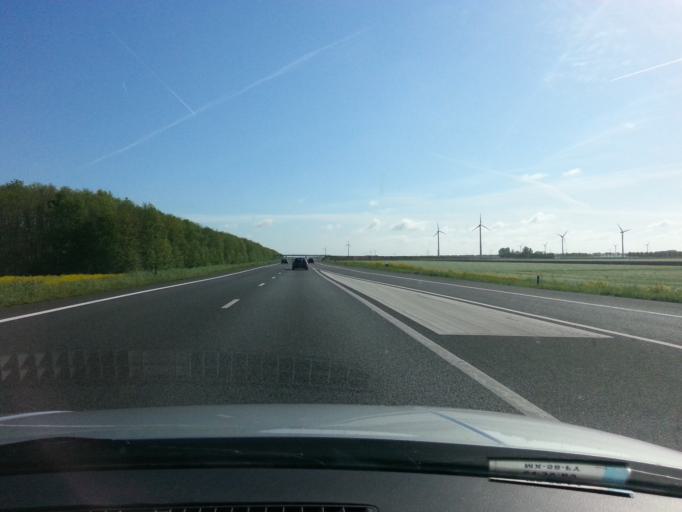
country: NL
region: Flevoland
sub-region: Gemeente Almere
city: Almere Stad
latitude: 52.4006
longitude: 5.3510
